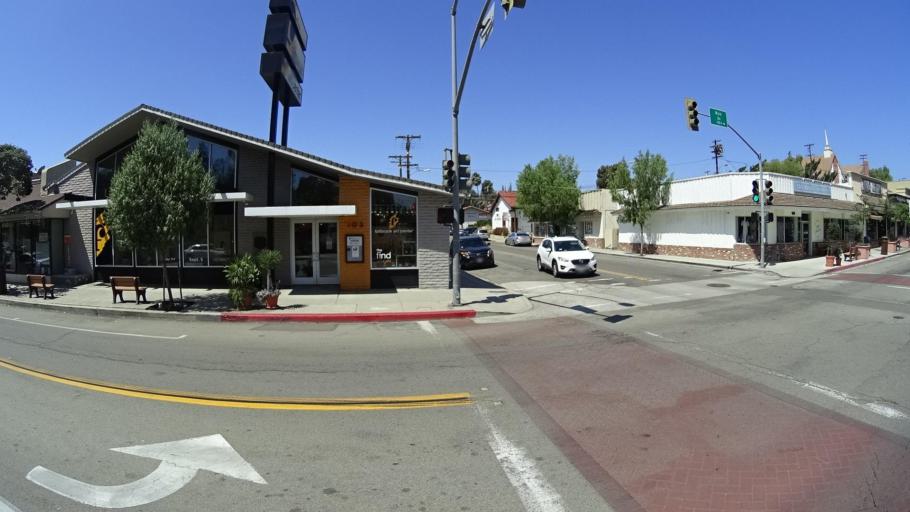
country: US
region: California
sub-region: San Diego County
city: Fallbrook
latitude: 33.3820
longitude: -117.2513
